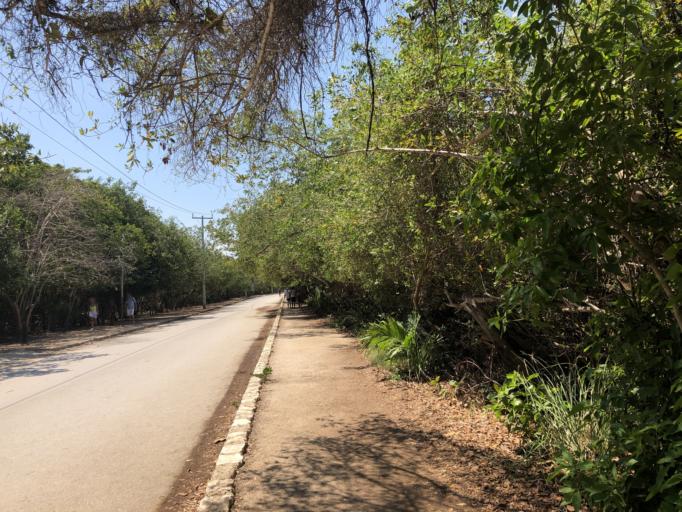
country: MX
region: Quintana Roo
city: Tulum
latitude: 20.2154
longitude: -87.4321
